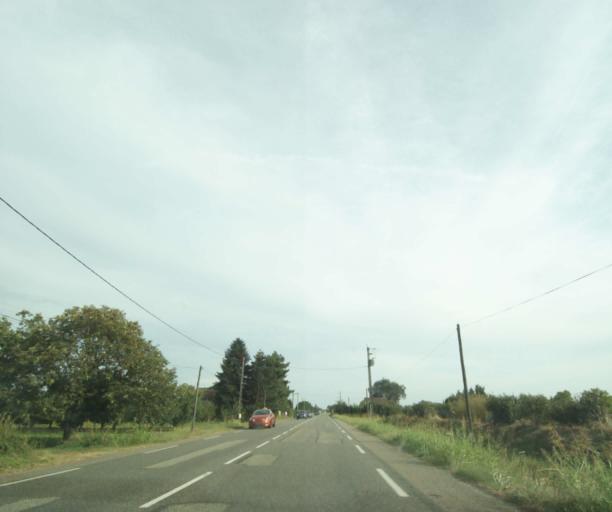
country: FR
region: Midi-Pyrenees
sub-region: Departement du Tarn-et-Garonne
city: Verdun-sur-Garonne
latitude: 43.8777
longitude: 1.2584
